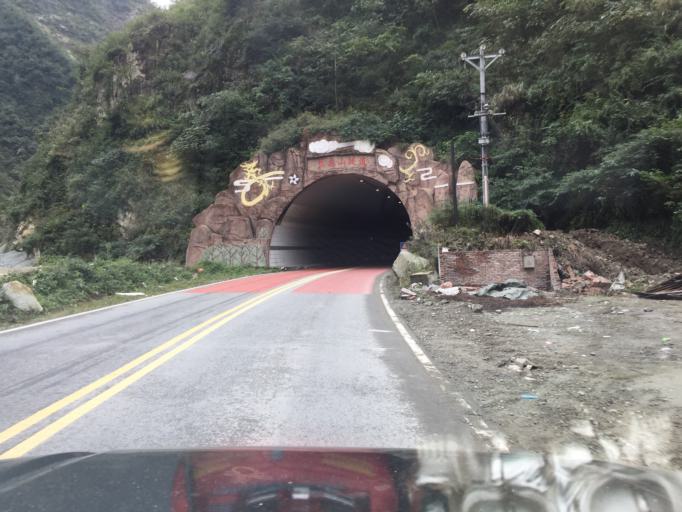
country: CN
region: Sichuan
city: Guangsheng
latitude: 31.0615
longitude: 103.4051
